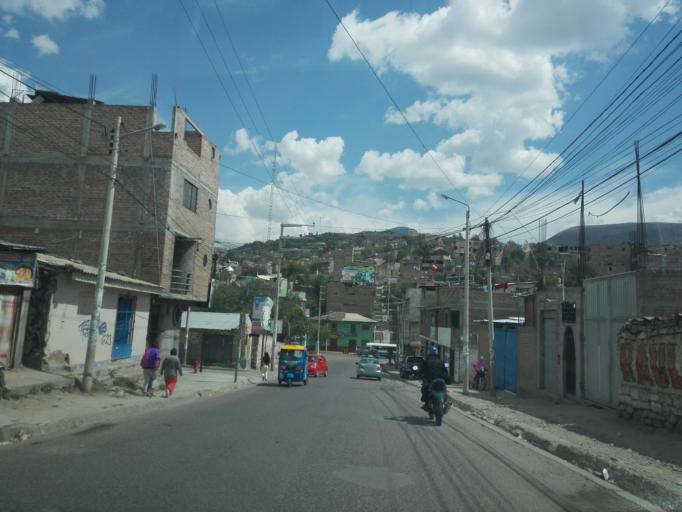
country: PE
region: Ayacucho
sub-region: Provincia de Huamanga
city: Ayacucho
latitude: -13.1641
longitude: -74.2164
